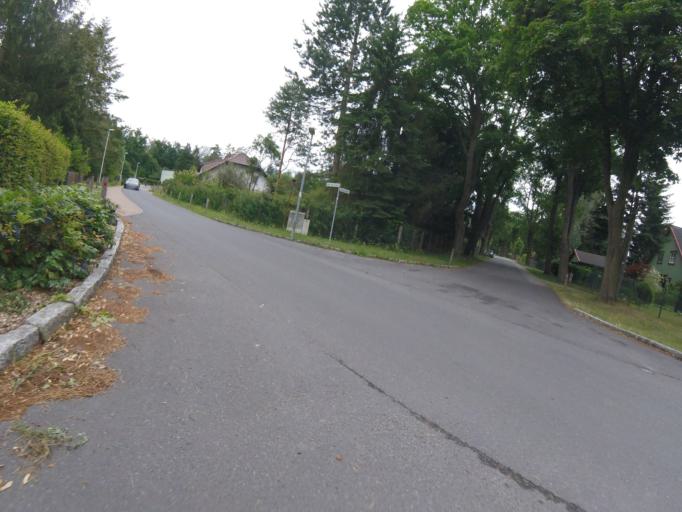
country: DE
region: Brandenburg
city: Bestensee
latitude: 52.2887
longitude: 13.7144
